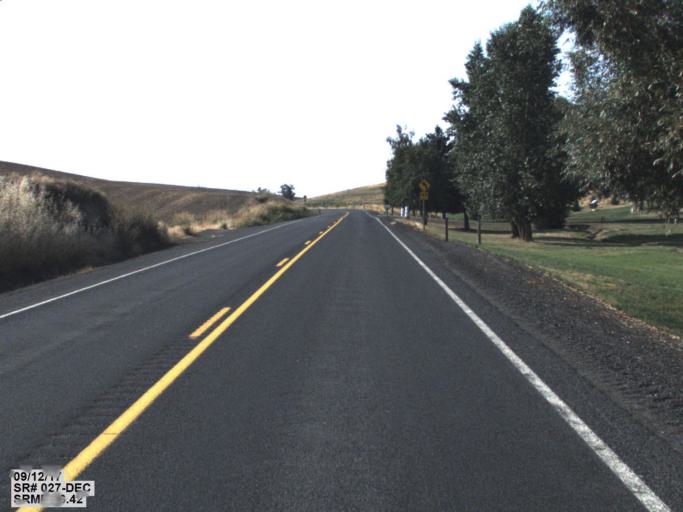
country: US
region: Idaho
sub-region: Benewah County
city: Plummer
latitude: 47.2022
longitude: -117.0922
